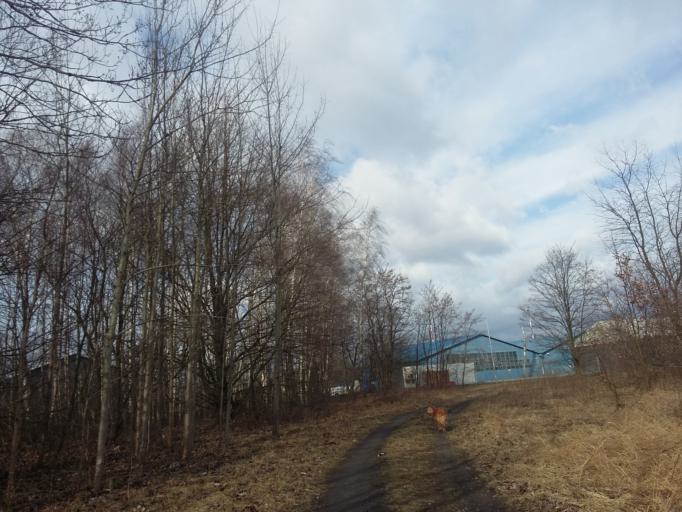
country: PL
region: Lodz Voivodeship
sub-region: Powiat pabianicki
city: Ksawerow
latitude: 51.7264
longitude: 19.4060
